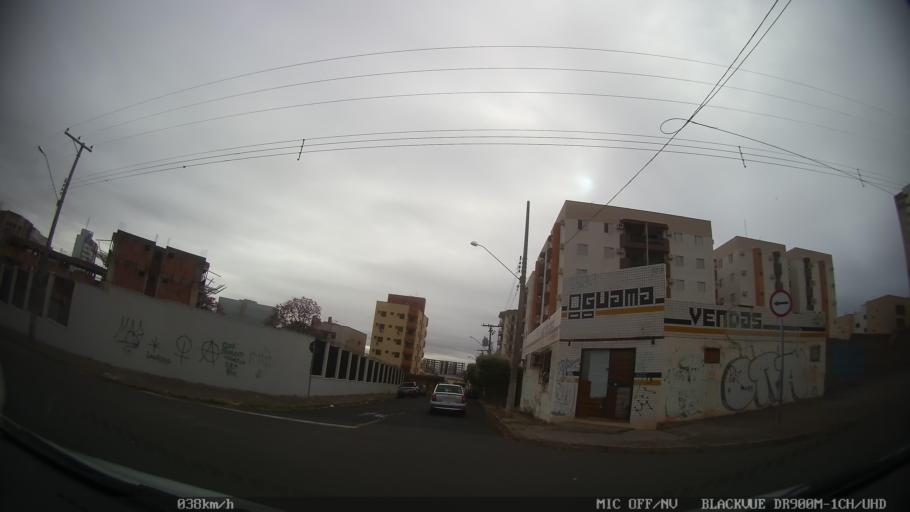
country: BR
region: Sao Paulo
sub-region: Sao Jose Do Rio Preto
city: Sao Jose do Rio Preto
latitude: -20.8312
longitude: -49.3892
